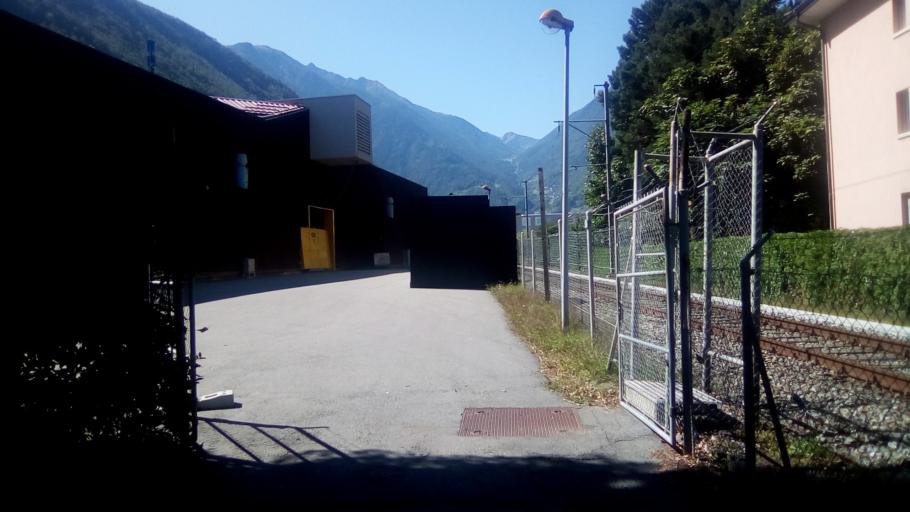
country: CH
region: Valais
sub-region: Martigny District
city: Martigny-Ville
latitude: 46.0991
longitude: 7.0783
